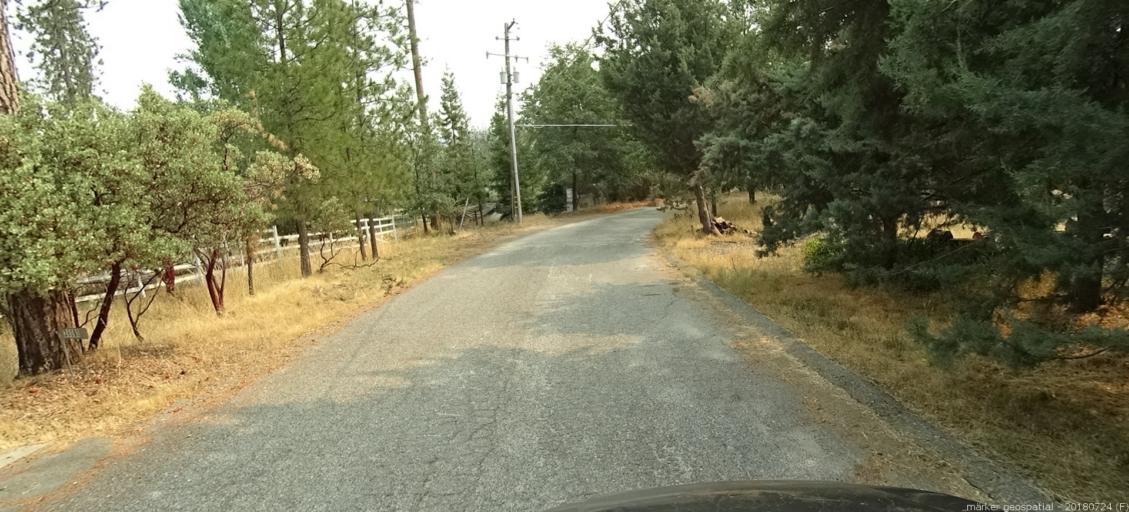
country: US
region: California
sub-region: Madera County
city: Oakhurst
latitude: 37.3018
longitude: -119.6038
